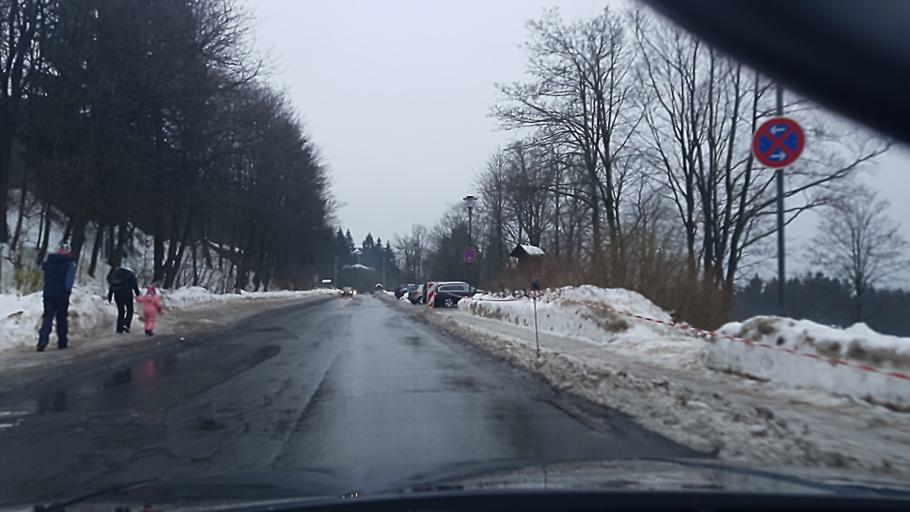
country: DE
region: Lower Saxony
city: Clausthal-Zellerfeld
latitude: 51.8576
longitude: 10.3381
